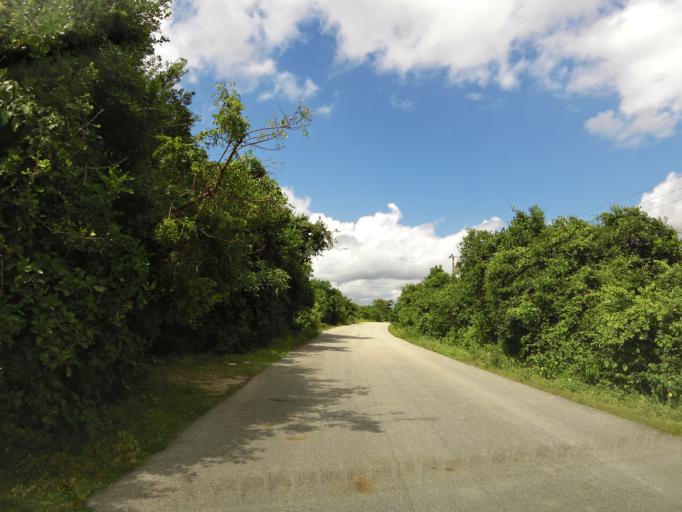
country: TZ
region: Zanzibar Central/South
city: Koani
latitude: -6.1461
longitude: 39.4275
